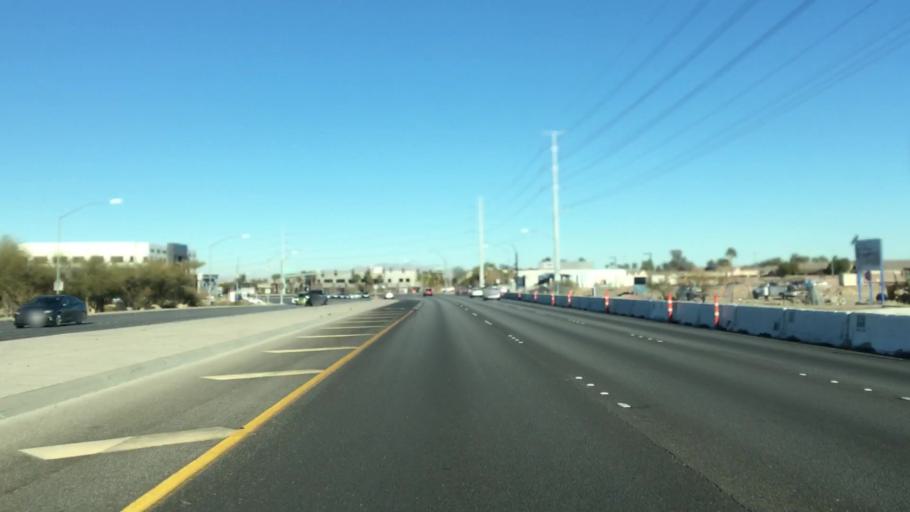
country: US
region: Nevada
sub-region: Clark County
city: Whitney
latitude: 36.0145
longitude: -115.1038
